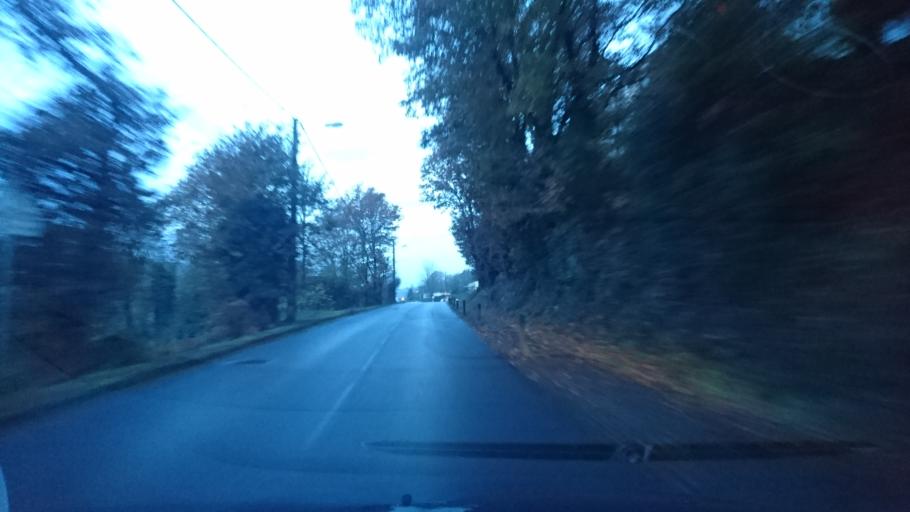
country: FR
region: Brittany
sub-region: Departement du Finistere
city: Chateaulin
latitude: 48.1908
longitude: -4.0844
